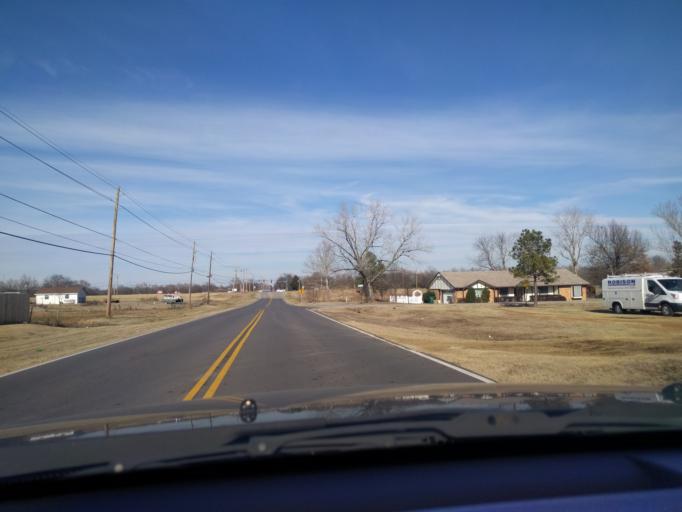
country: US
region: Oklahoma
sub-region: Tulsa County
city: Broken Arrow
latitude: 36.0581
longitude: -95.7081
